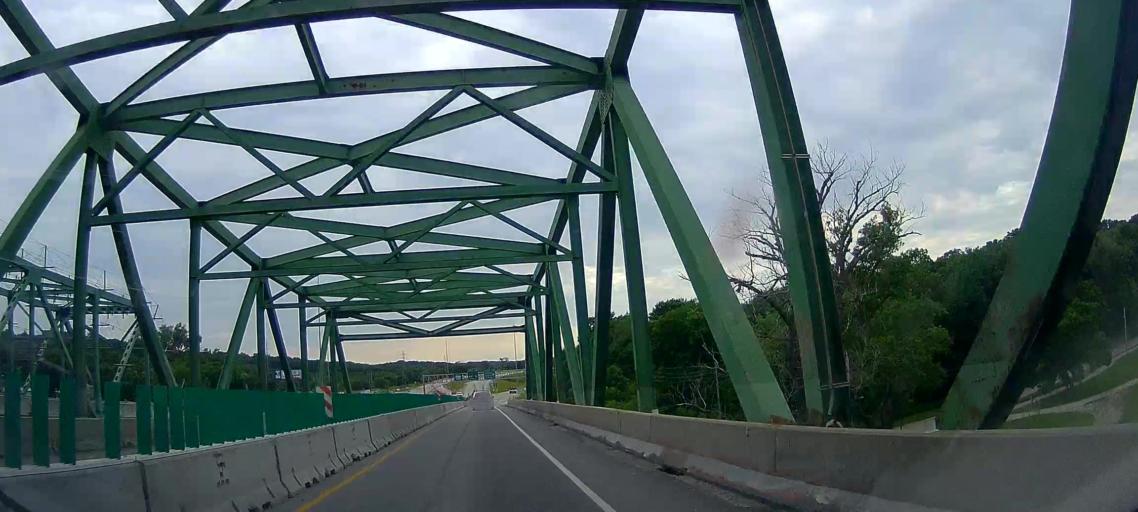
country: US
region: Iowa
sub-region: Pottawattamie County
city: Carter Lake
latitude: 41.3456
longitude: -95.9589
